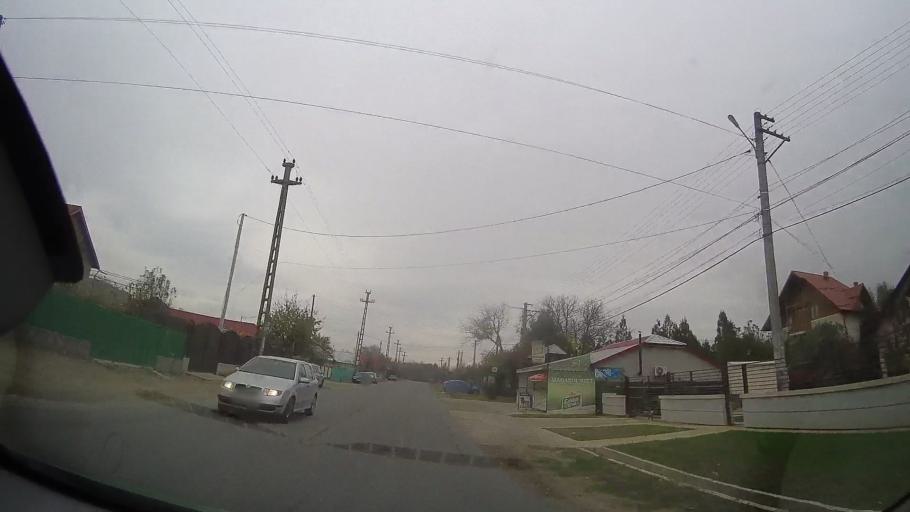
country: RO
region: Prahova
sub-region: Oras Urlati
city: Urlati
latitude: 45.0041
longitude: 26.2274
